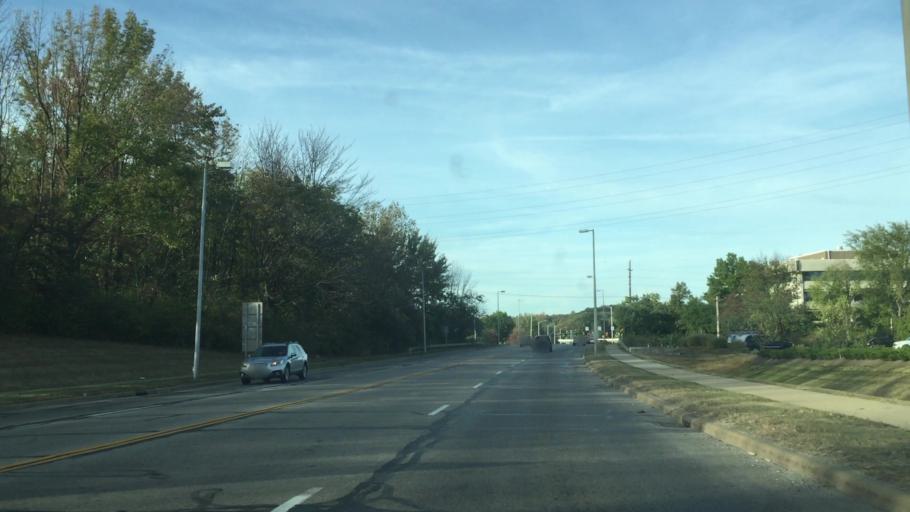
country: US
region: Ohio
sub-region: Cuyahoga County
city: Solon
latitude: 41.4007
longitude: -81.4686
